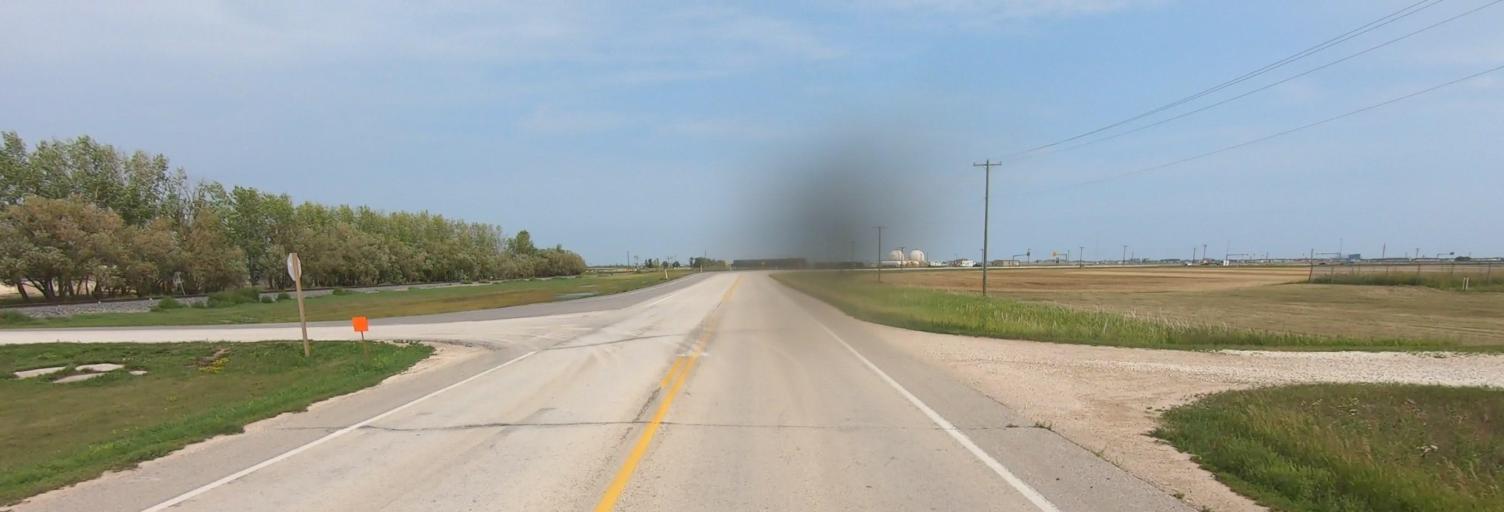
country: CA
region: Manitoba
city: Winnipeg
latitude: 49.7644
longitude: -97.2384
